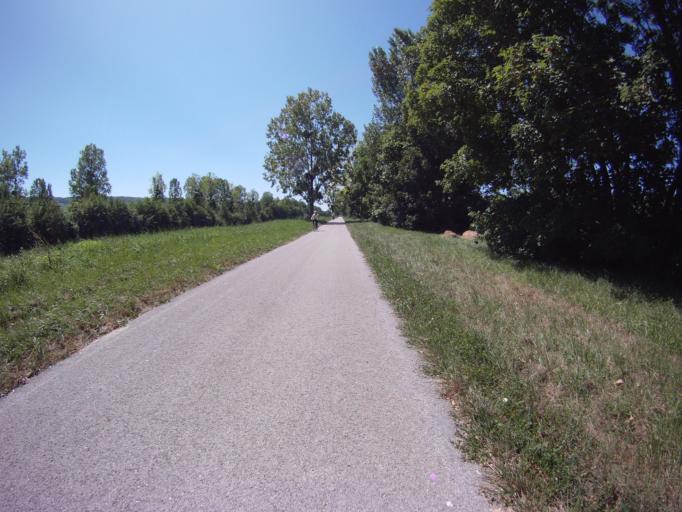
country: FR
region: Champagne-Ardenne
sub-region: Departement de la Marne
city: Damery
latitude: 49.0738
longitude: 3.8586
